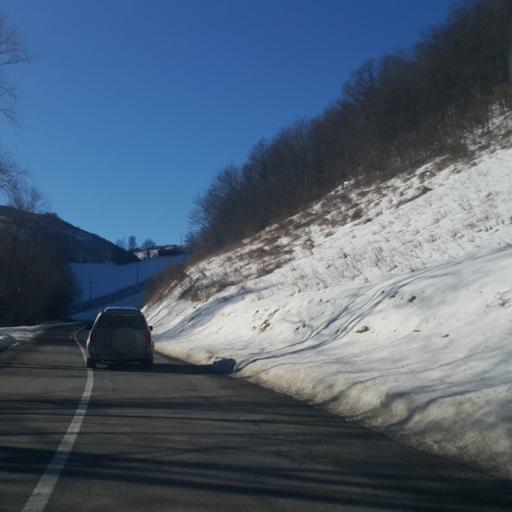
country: RS
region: Central Serbia
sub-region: Rasinski Okrug
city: Aleksandrovac
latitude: 43.3223
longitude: 20.9208
